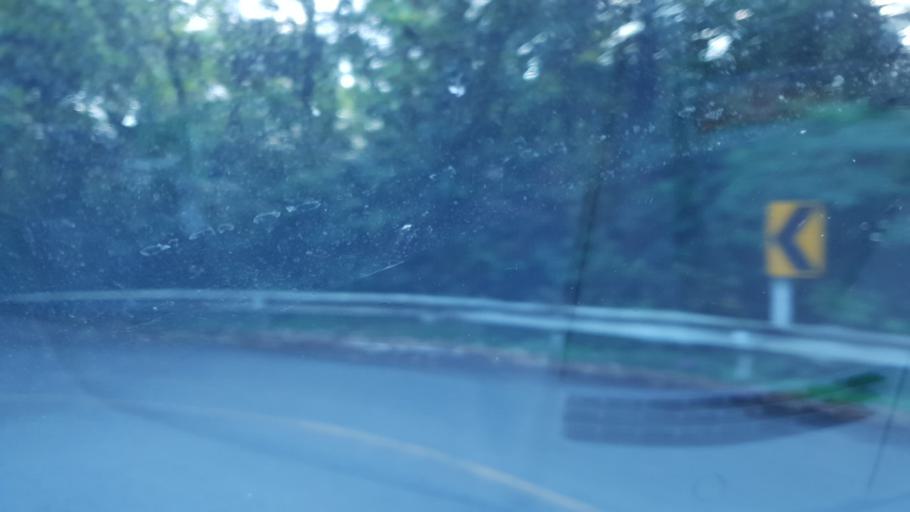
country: TH
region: Chiang Mai
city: Mae Chaem
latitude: 18.5246
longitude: 98.4872
